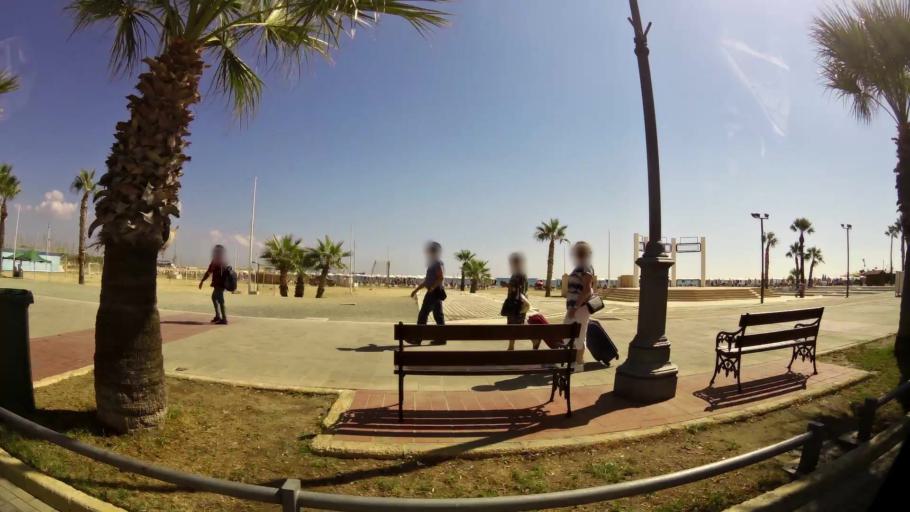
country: CY
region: Larnaka
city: Larnaca
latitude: 34.9150
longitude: 33.6381
